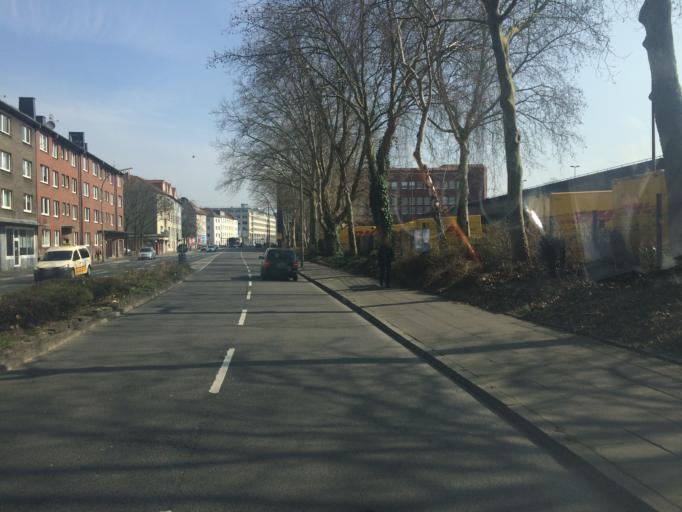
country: DE
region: North Rhine-Westphalia
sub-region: Regierungsbezirk Arnsberg
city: Dortmund
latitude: 51.5193
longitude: 7.4537
